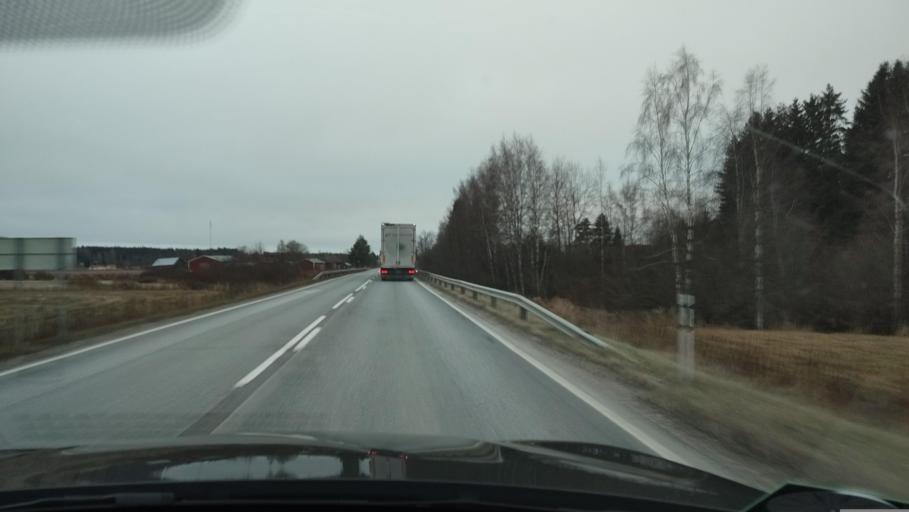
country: FI
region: Southern Ostrobothnia
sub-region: Suupohja
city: Kauhajoki
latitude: 62.3677
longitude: 22.0759
